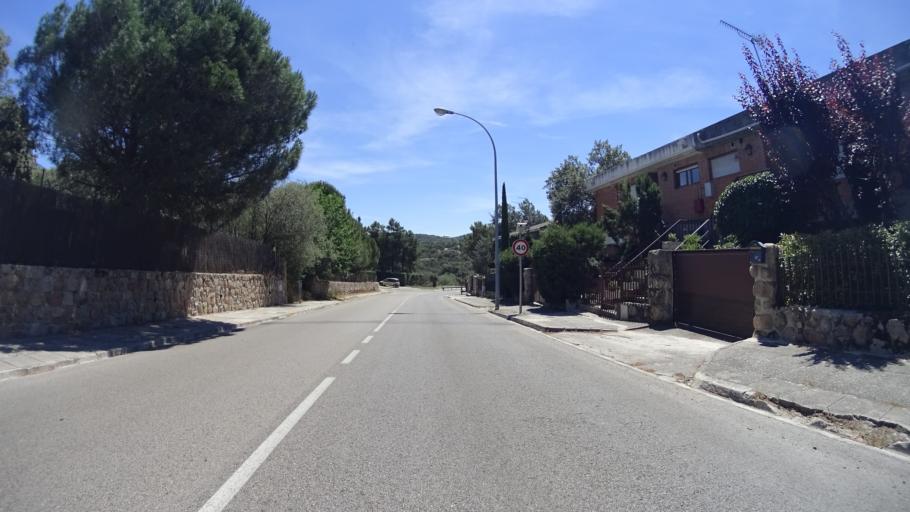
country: ES
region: Madrid
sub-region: Provincia de Madrid
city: Torrelodones
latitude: 40.6055
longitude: -3.9401
